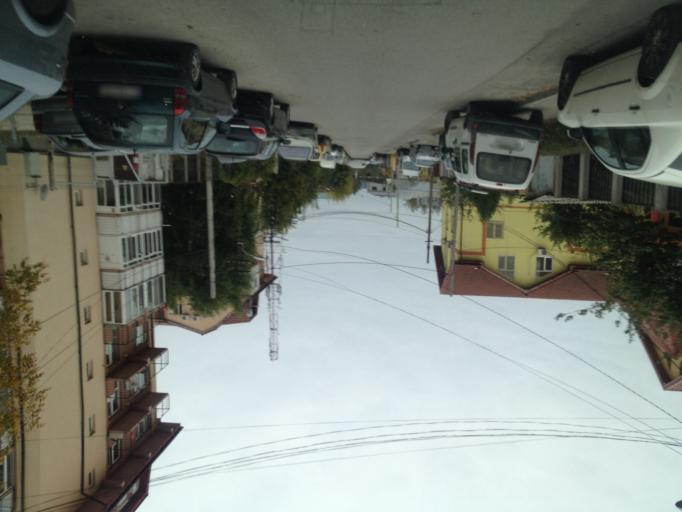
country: RO
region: Dolj
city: Craiova
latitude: 44.3344
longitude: 23.7749
